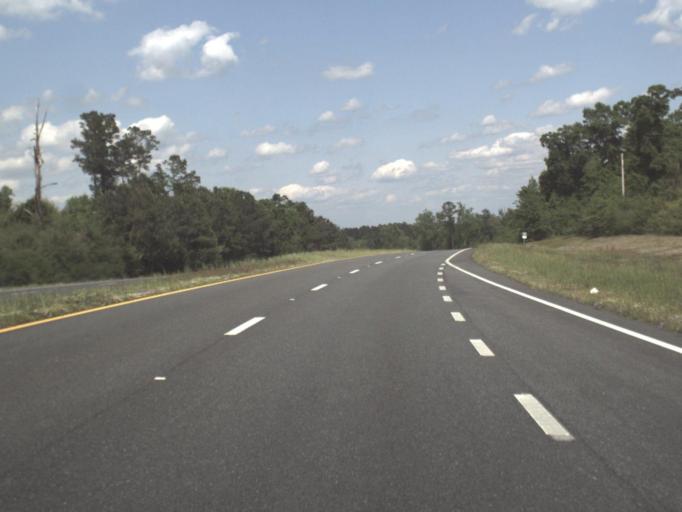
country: US
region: Florida
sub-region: Escambia County
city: Century
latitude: 30.9311
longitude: -87.3002
